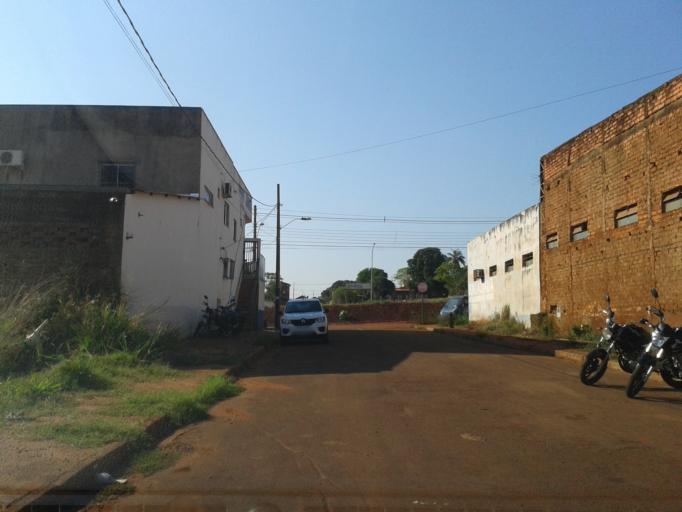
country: BR
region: Minas Gerais
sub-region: Ituiutaba
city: Ituiutaba
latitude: -18.9473
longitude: -49.4607
